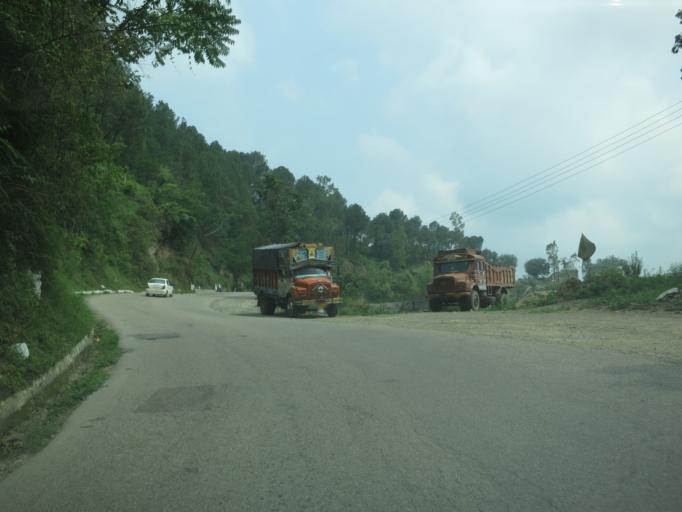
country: IN
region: Himachal Pradesh
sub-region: Bilaspur
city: Bilaspur
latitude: 31.2576
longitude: 76.8700
